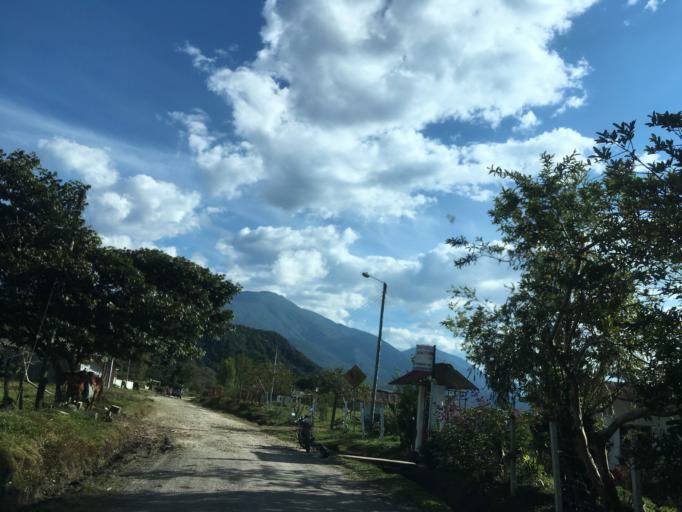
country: CO
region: Santander
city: Oiba
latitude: 6.1067
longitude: -73.1974
